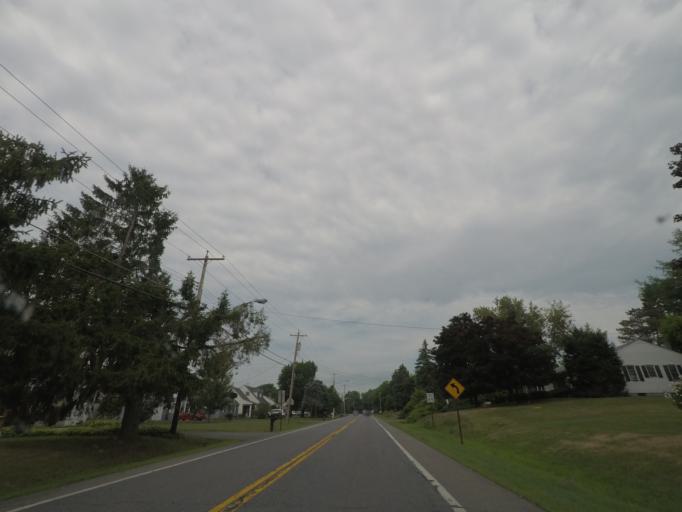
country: US
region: New York
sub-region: Saratoga County
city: Waterford
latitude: 42.8125
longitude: -73.6868
